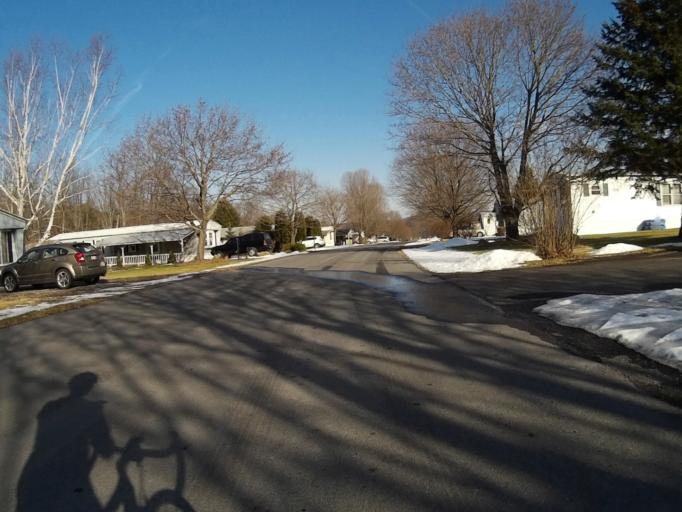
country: US
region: Pennsylvania
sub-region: Centre County
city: Houserville
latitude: 40.8727
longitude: -77.8715
